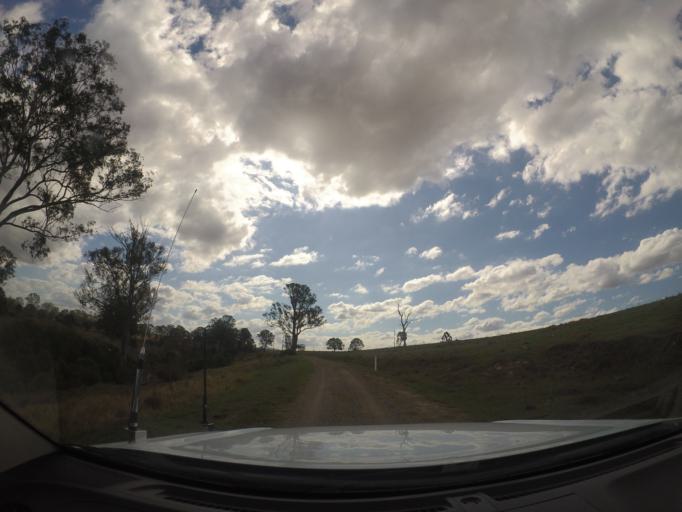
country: AU
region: Queensland
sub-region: Logan
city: North Maclean
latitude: -27.8091
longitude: 153.0097
